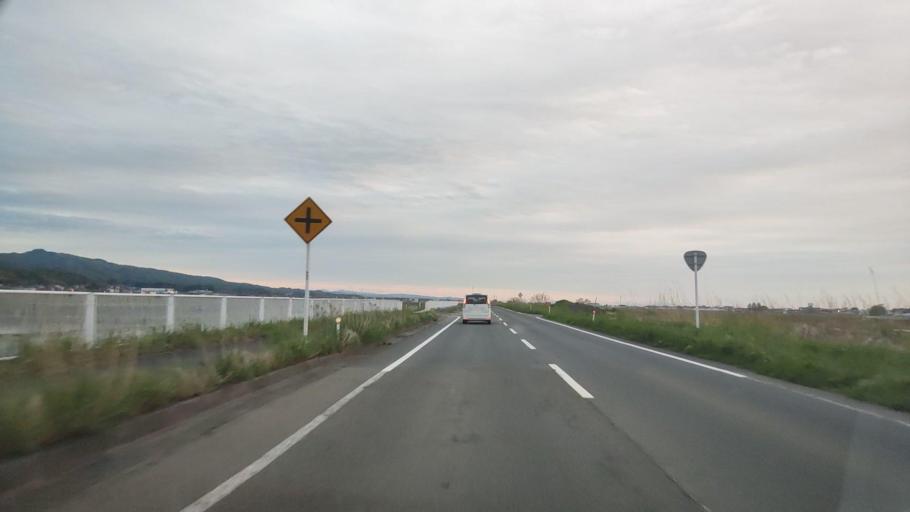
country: JP
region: Niigata
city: Niitsu-honcho
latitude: 37.7639
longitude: 139.0974
